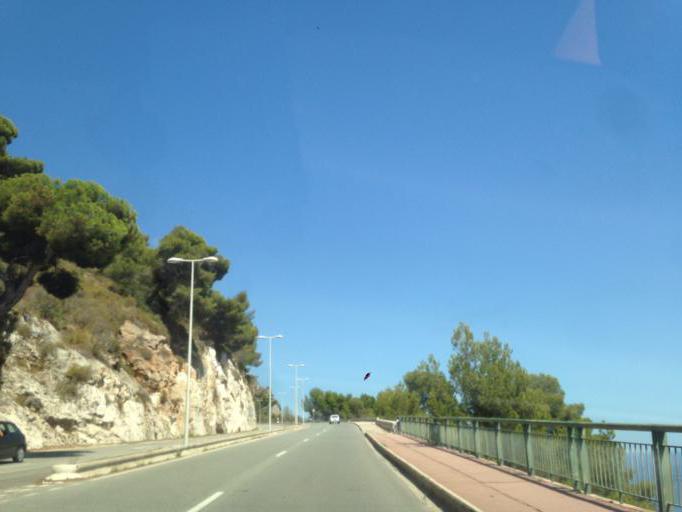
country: FR
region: Provence-Alpes-Cote d'Azur
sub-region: Departement des Alpes-Maritimes
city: Beaulieu-sur-Mer
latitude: 43.7126
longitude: 7.3262
